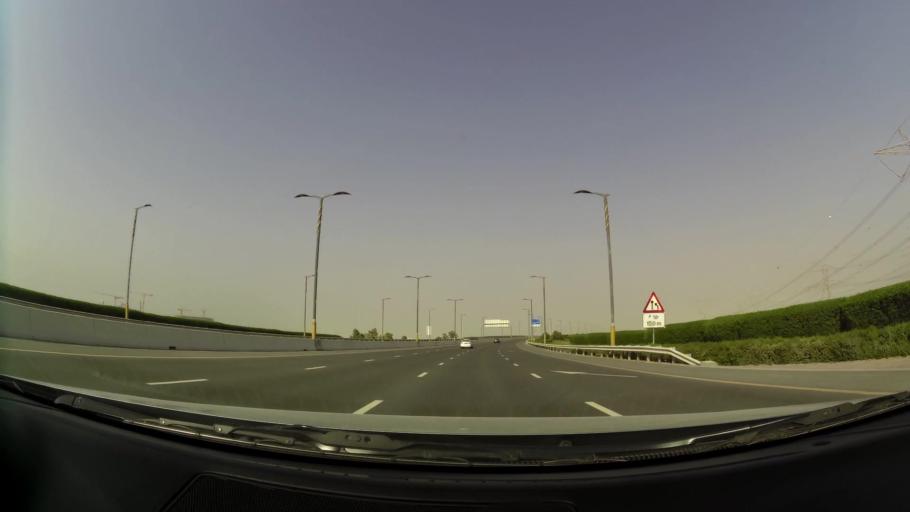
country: AE
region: Dubai
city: Dubai
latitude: 25.1704
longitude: 55.3079
